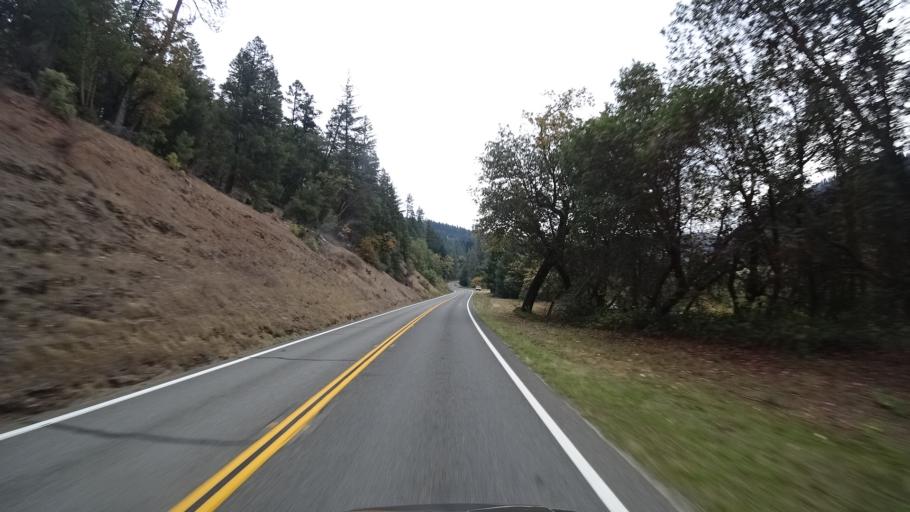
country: US
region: California
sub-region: Siskiyou County
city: Happy Camp
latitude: 41.8094
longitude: -123.3507
